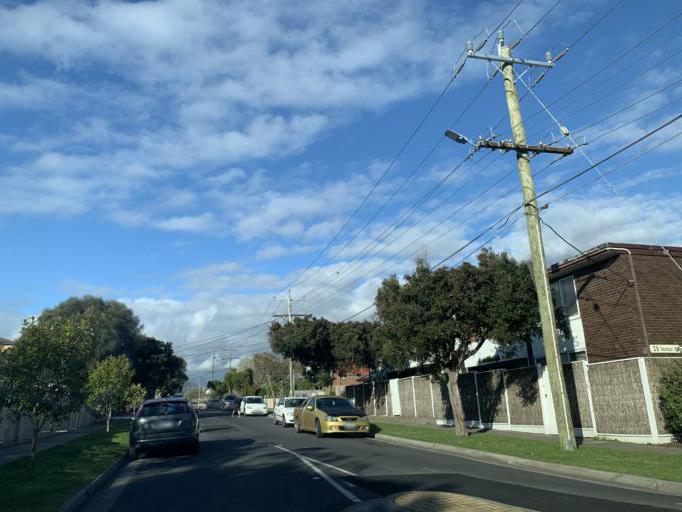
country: AU
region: Victoria
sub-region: Kingston
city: Mentone
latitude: -37.9863
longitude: 145.0662
